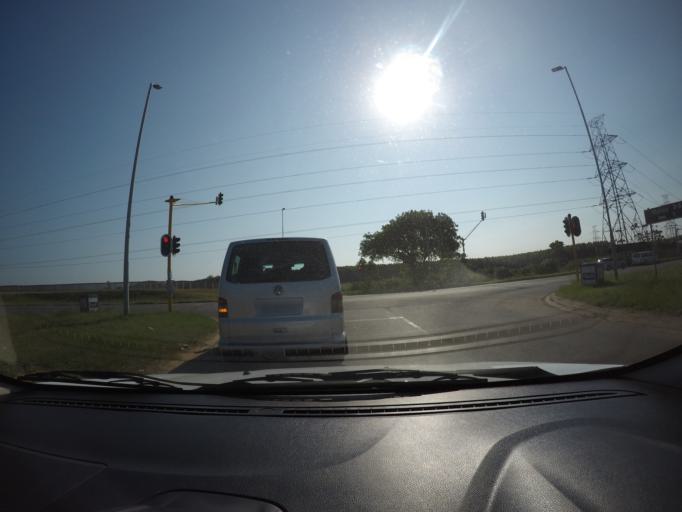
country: ZA
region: KwaZulu-Natal
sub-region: uThungulu District Municipality
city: Richards Bay
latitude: -28.7253
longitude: 32.0356
